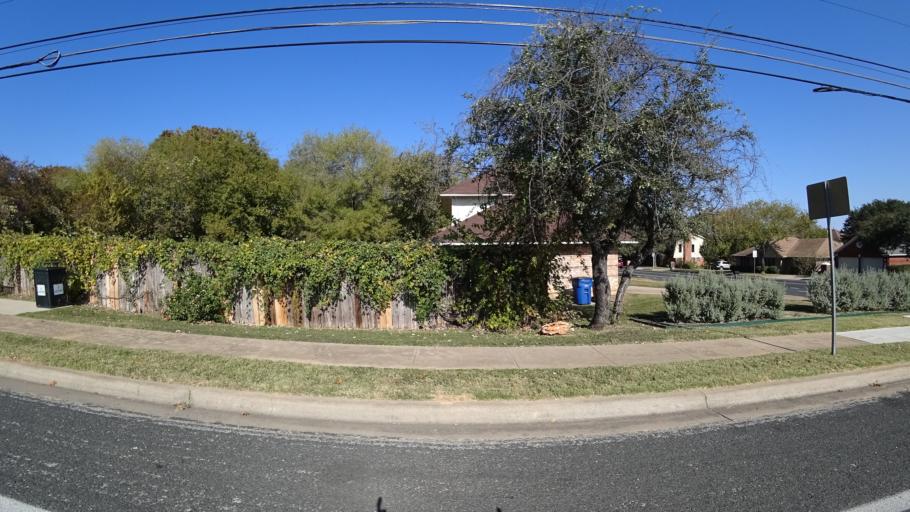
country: US
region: Texas
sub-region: Travis County
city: Shady Hollow
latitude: 30.2206
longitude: -97.8580
